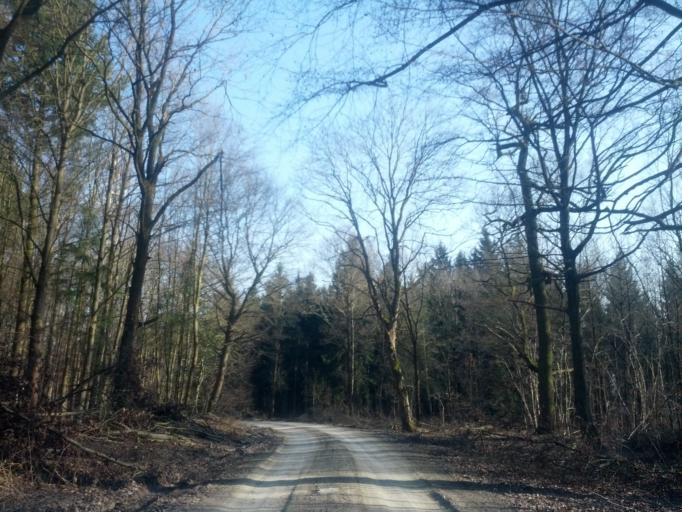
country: DE
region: Thuringia
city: Ebenshausen
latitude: 51.0811
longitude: 10.3073
